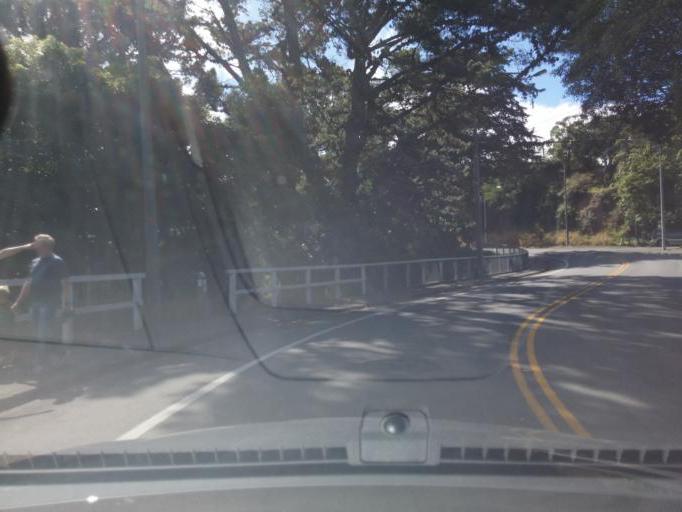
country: NZ
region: Wellington
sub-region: Wellington City
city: Kelburn
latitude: -41.2569
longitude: 174.7733
